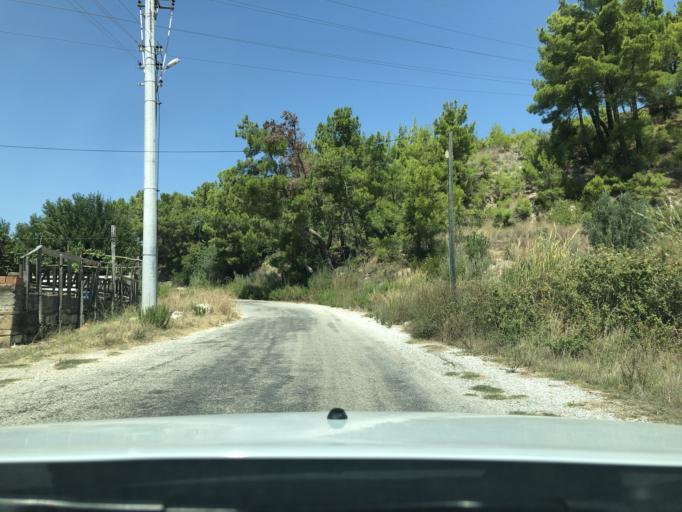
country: TR
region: Antalya
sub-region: Manavgat
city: Kizilagac
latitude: 36.8622
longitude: 31.5642
